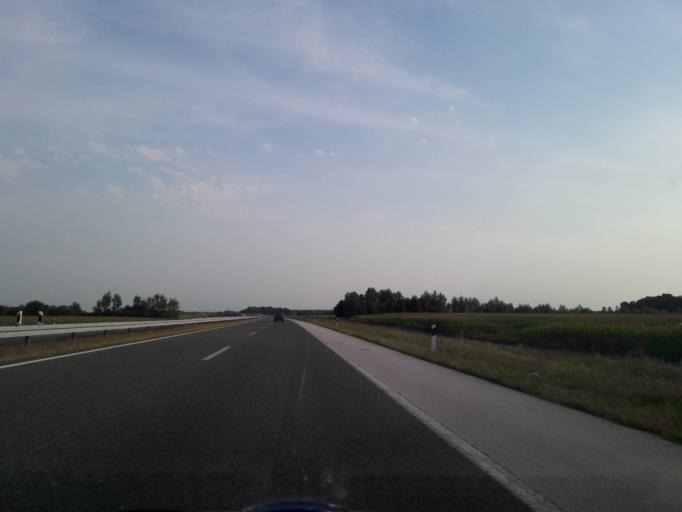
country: HR
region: Osjecko-Baranjska
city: Piskorevci
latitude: 45.2360
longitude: 18.3307
